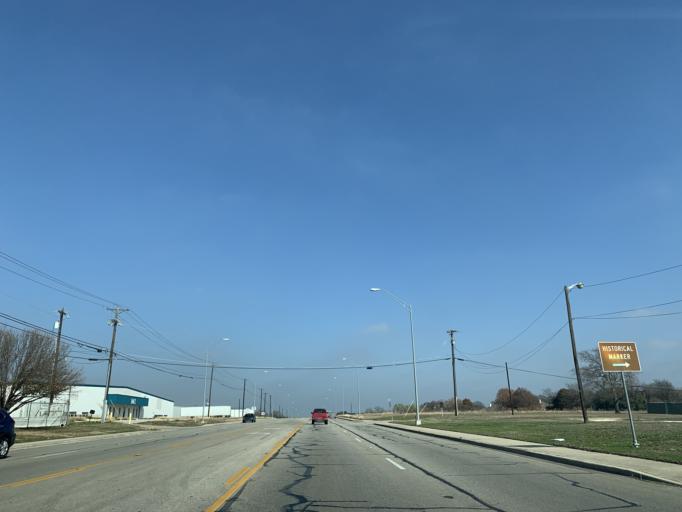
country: US
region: Texas
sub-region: Williamson County
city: Round Rock
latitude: 30.5243
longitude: -97.6542
